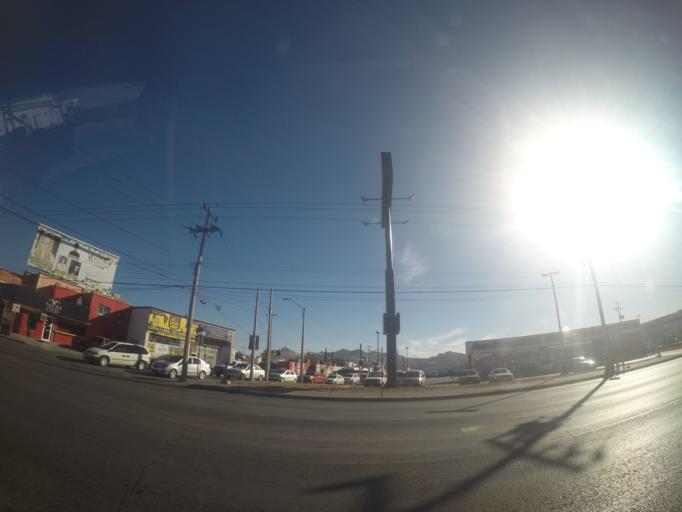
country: MX
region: Chihuahua
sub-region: Chihuahua
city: Chihuahua
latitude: 28.6715
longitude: -106.0968
